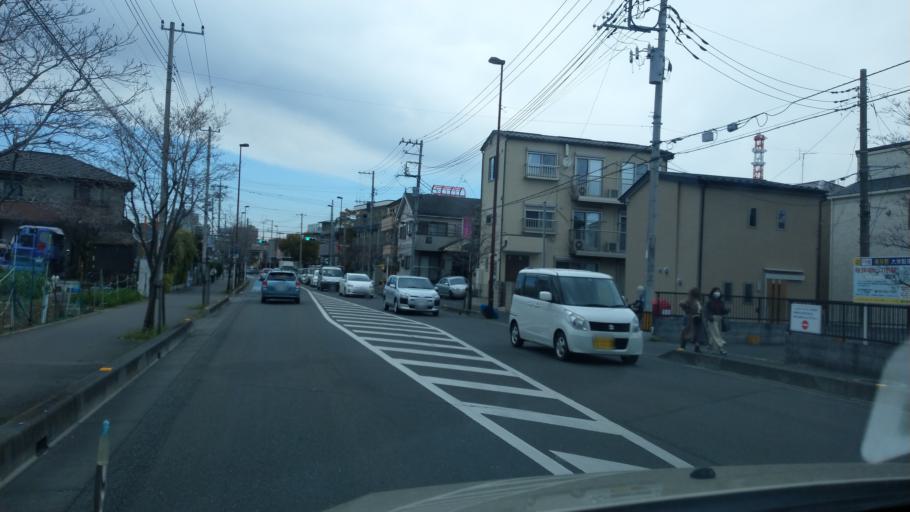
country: JP
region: Saitama
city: Yono
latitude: 35.8707
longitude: 139.6332
